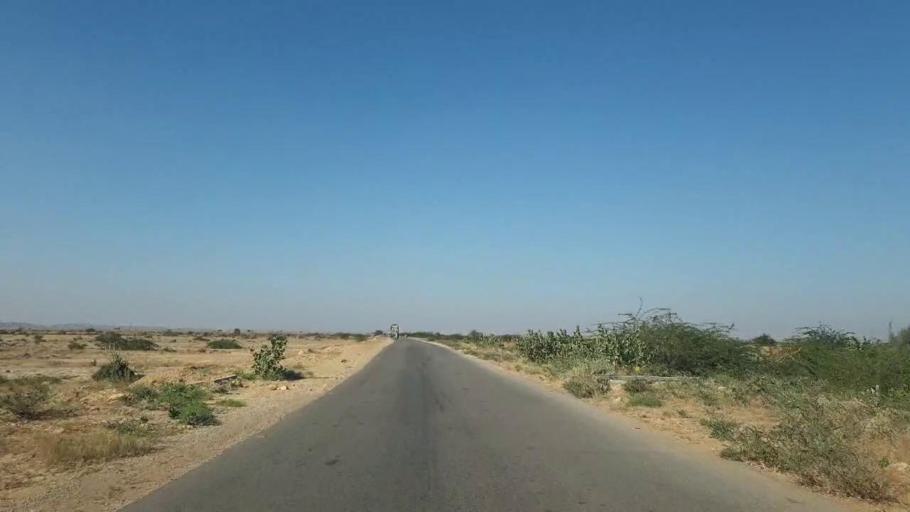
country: PK
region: Sindh
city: Malir Cantonment
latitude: 25.2497
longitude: 67.6043
